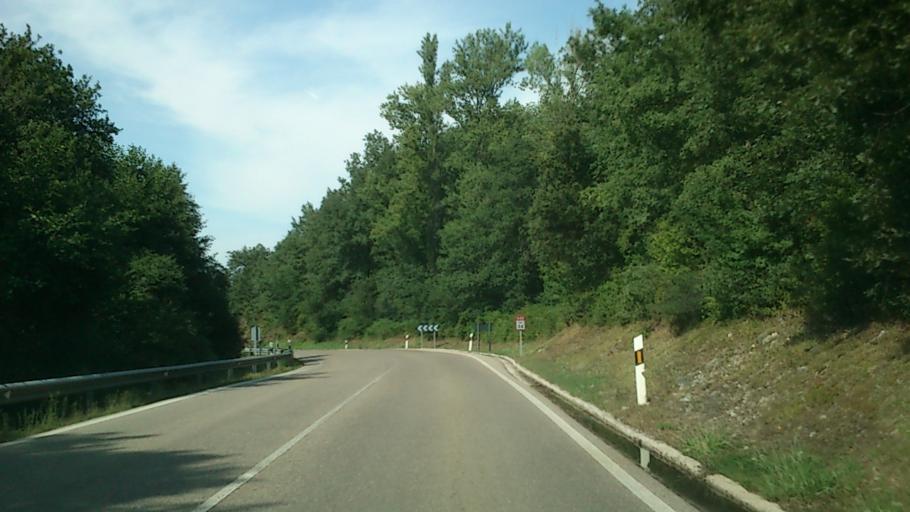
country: ES
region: Castille and Leon
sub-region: Provincia de Burgos
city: Medina de Pomar
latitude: 43.0190
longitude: -3.4834
